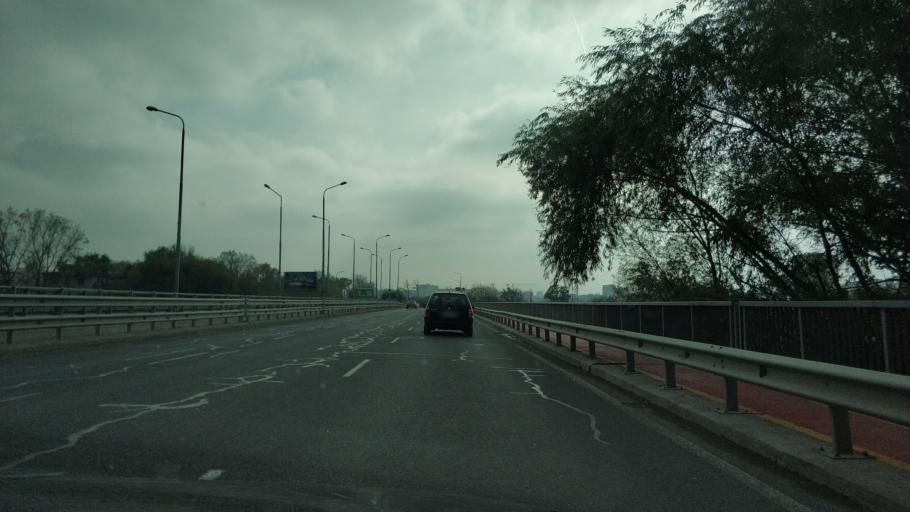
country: BG
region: Plovdiv
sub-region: Obshtina Plovdiv
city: Plovdiv
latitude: 42.1551
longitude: 24.7655
